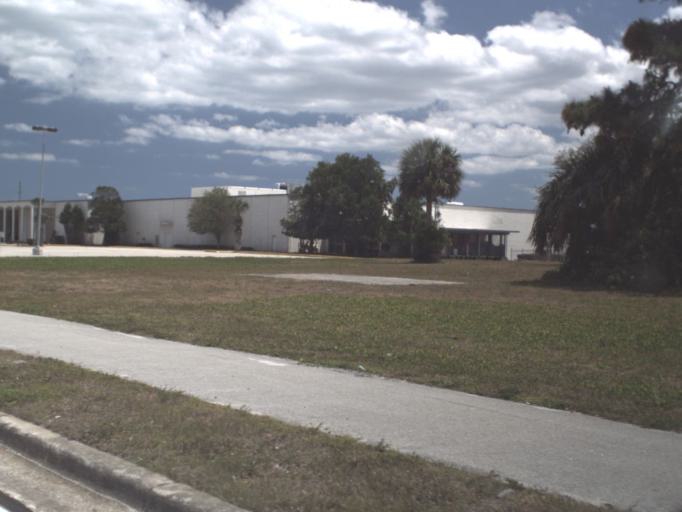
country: US
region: Florida
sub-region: Brevard County
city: Melbourne
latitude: 28.0933
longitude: -80.6255
